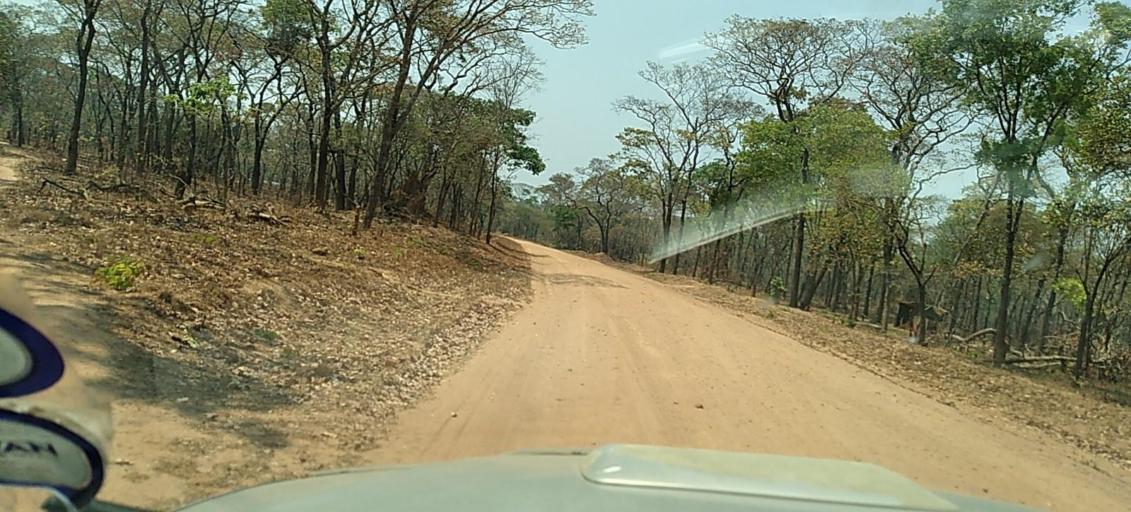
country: ZM
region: North-Western
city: Kasempa
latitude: -13.5476
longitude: 26.0518
